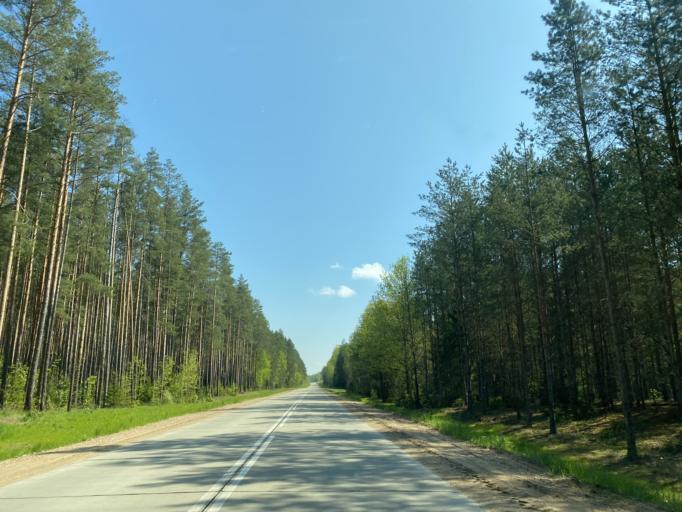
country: BY
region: Minsk
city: Horad Barysaw
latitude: 54.1726
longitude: 28.5241
